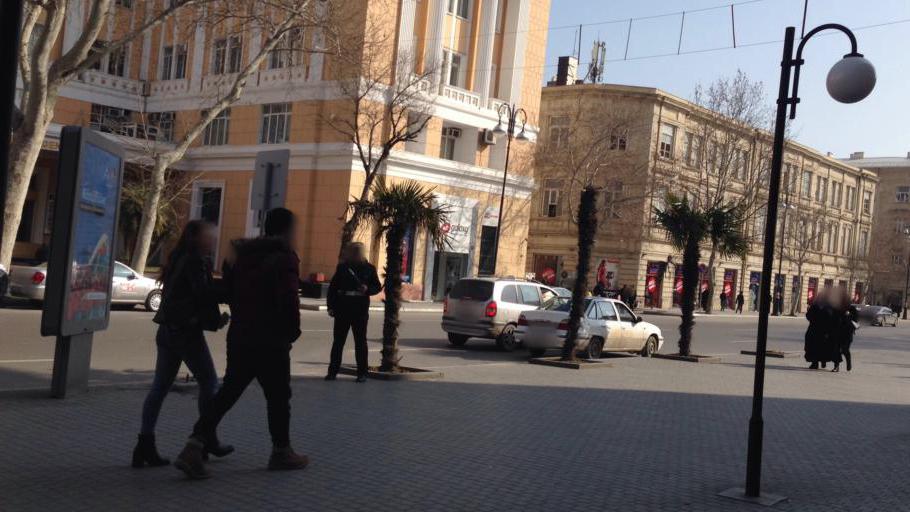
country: AZ
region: Baki
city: Baku
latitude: 40.3748
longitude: 49.8431
